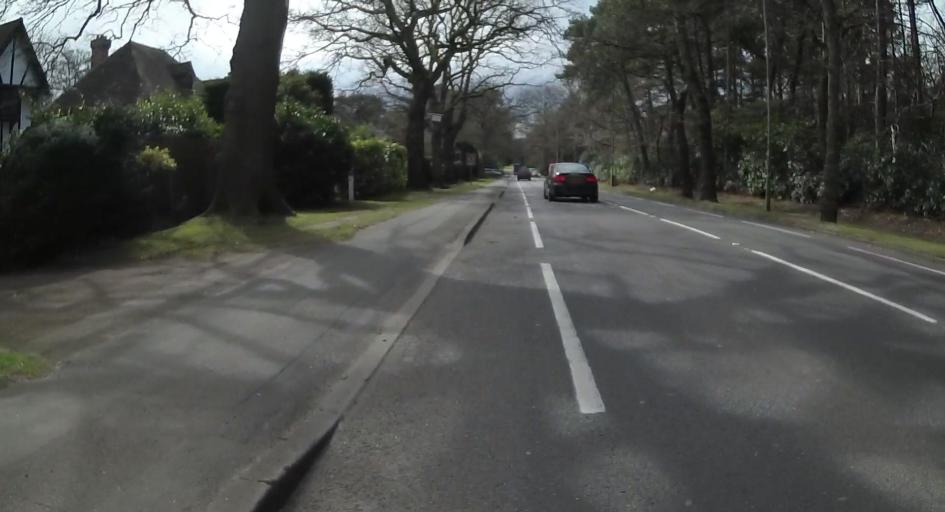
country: GB
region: England
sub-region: Surrey
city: Woking
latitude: 51.3349
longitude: -0.5411
